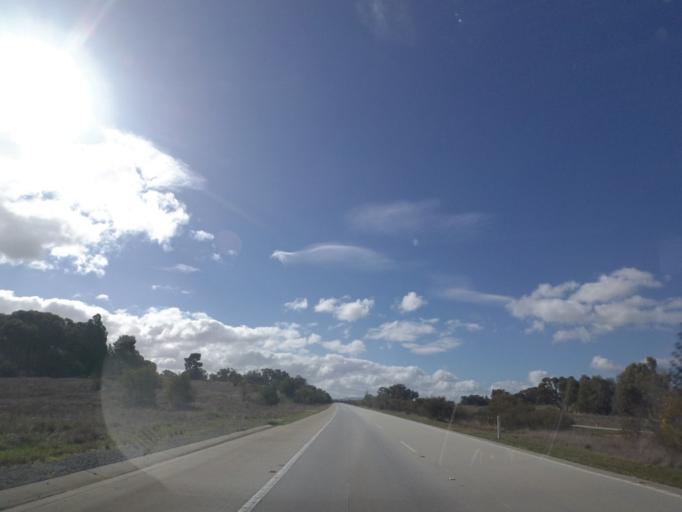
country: AU
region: New South Wales
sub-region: Albury Municipality
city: Lavington
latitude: -36.0164
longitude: 146.9852
